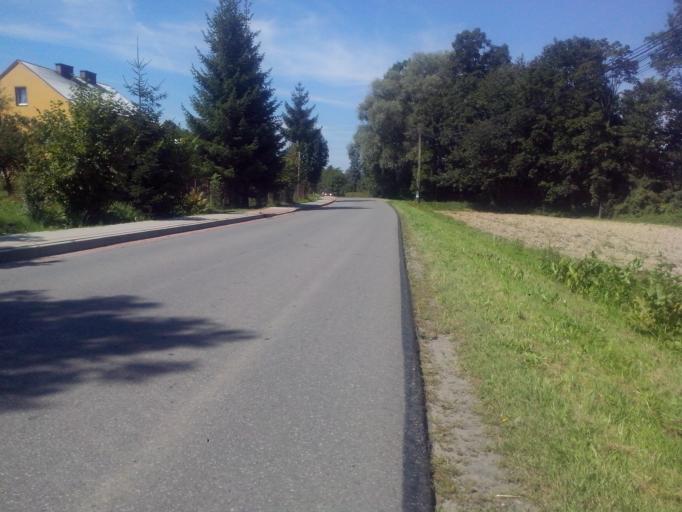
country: PL
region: Subcarpathian Voivodeship
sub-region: Powiat strzyzowski
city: Frysztak
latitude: 49.8650
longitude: 21.6216
